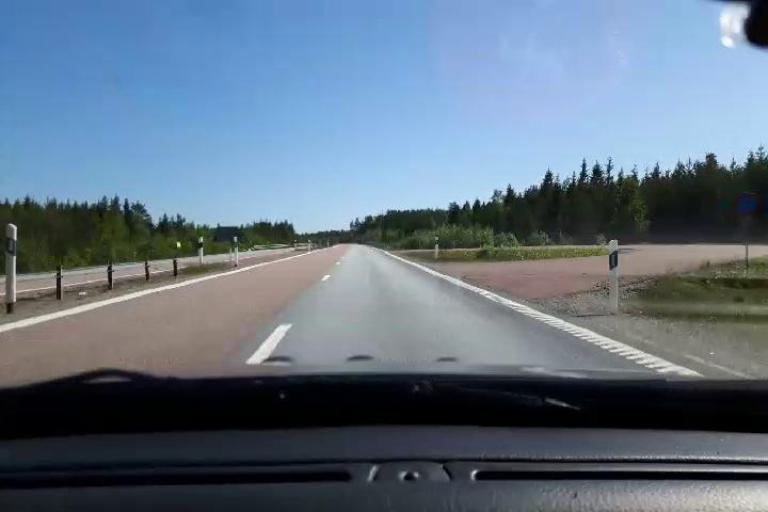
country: SE
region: Gaevleborg
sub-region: Soderhamns Kommun
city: Soderhamn
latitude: 61.4230
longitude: 16.9846
